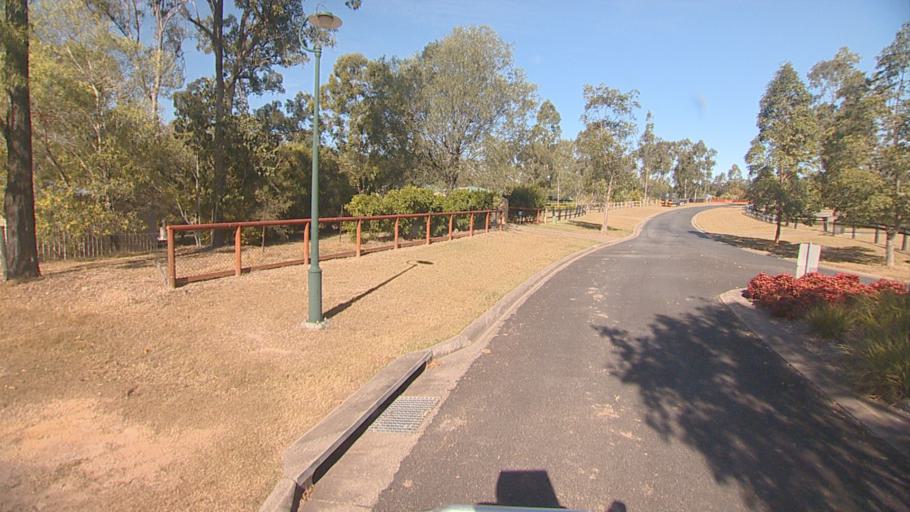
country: AU
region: Queensland
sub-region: Logan
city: North Maclean
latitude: -27.7975
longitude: 152.9743
